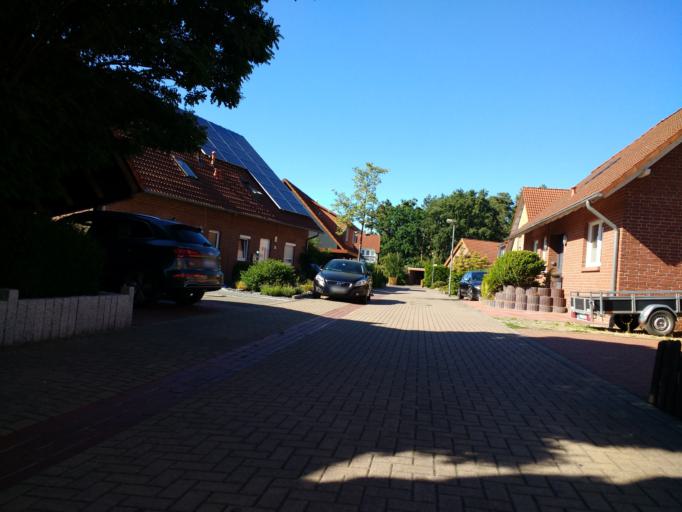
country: DE
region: Lower Saxony
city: Gifhorn
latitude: 52.4629
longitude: 10.5640
